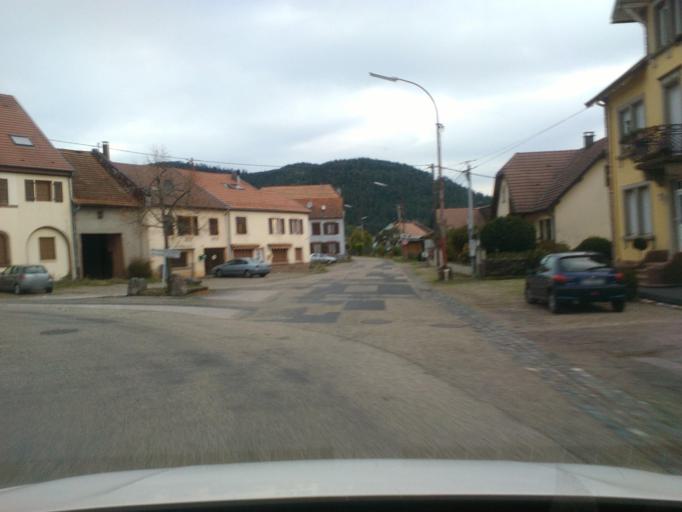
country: FR
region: Lorraine
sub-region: Departement des Vosges
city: Ban-de-Laveline
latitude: 48.3495
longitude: 7.1066
